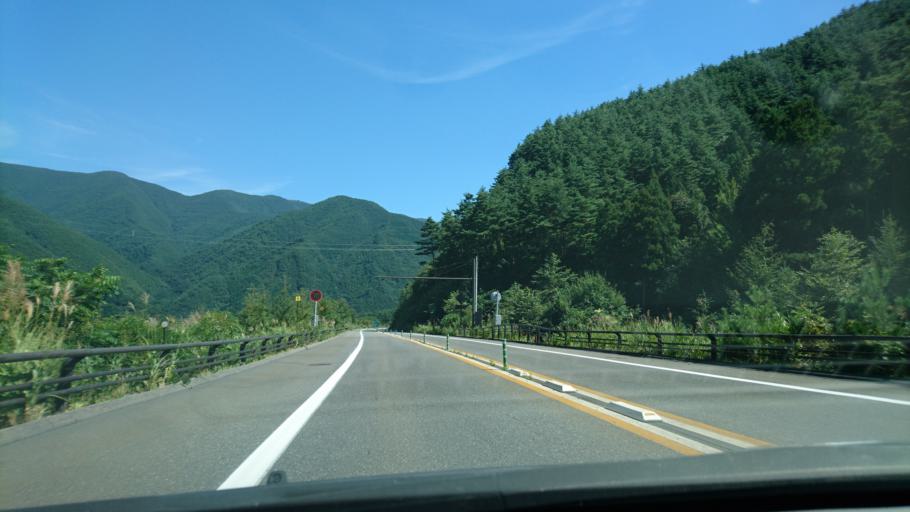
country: JP
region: Iwate
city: Kamaishi
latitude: 39.2463
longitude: 141.7439
